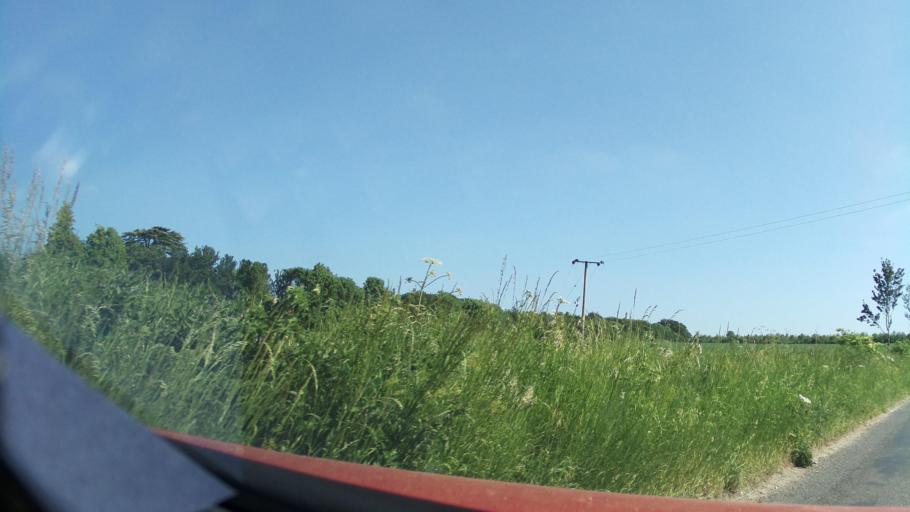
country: GB
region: England
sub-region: Hampshire
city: Abbotts Ann
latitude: 51.2282
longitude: -1.5651
